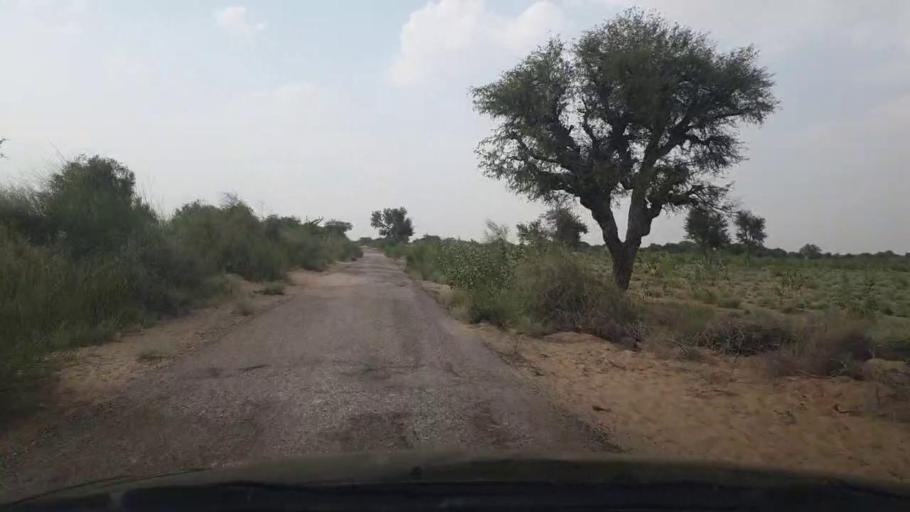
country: PK
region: Sindh
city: Islamkot
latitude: 24.9822
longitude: 70.5814
